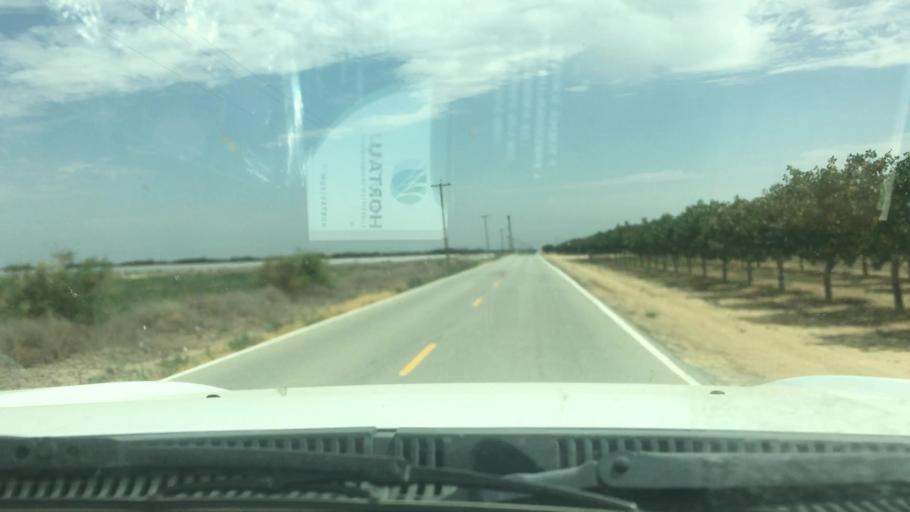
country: US
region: California
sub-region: Kern County
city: Lost Hills
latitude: 35.6353
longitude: -119.5802
